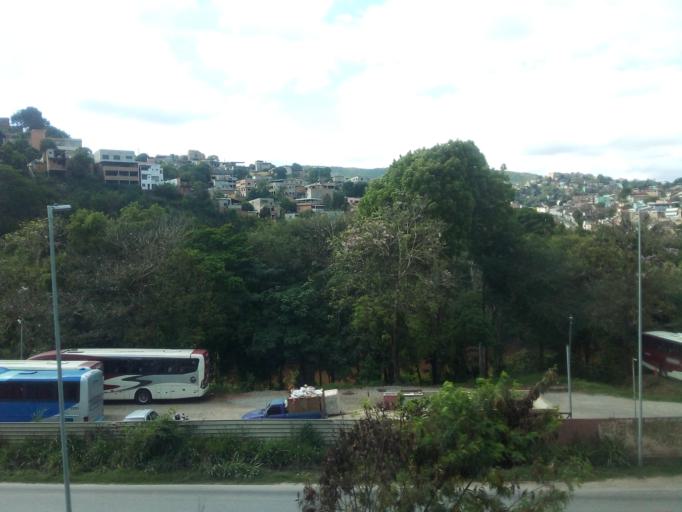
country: BR
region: Minas Gerais
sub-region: Belo Horizonte
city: Belo Horizonte
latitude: -19.8753
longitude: -43.8554
